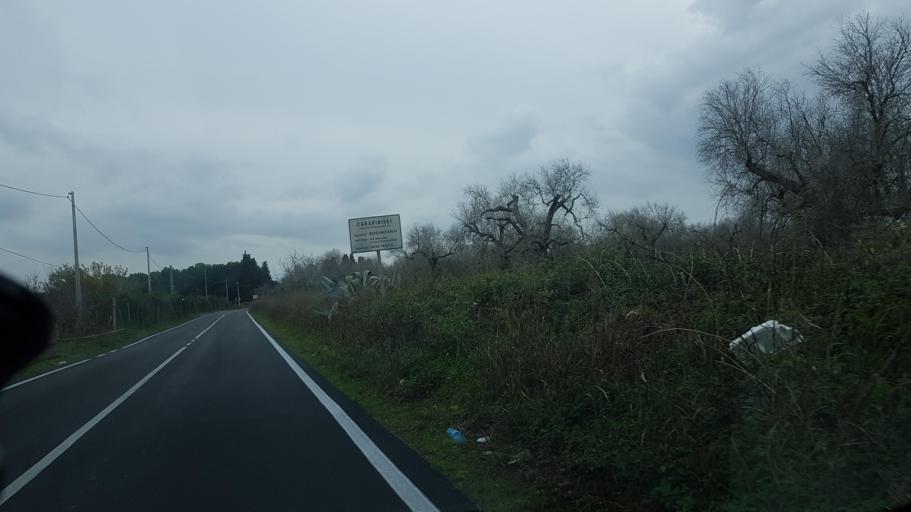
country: IT
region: Apulia
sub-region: Provincia di Lecce
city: Squinzano
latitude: 40.4457
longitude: 18.0478
